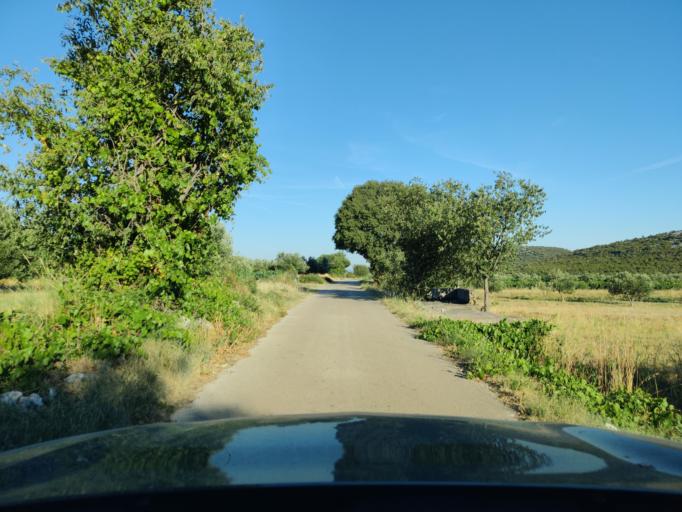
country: HR
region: Sibensko-Kniniska
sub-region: Grad Sibenik
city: Pirovac
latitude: 43.8626
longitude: 15.7015
